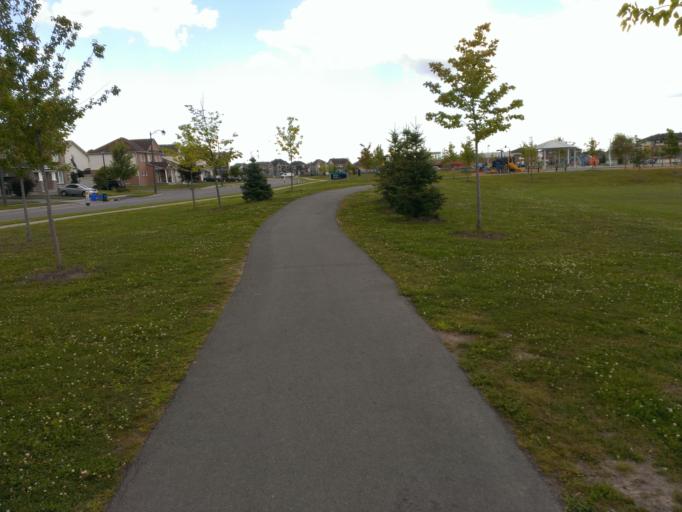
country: CA
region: Ontario
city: Clarence-Rockland
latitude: 45.4500
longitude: -75.4733
